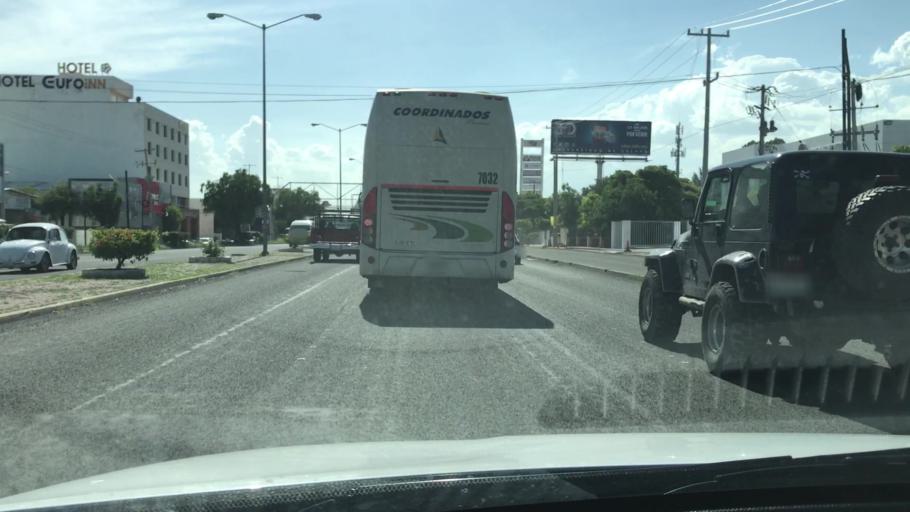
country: MX
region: Guanajuato
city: Celaya
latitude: 20.5167
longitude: -100.7852
